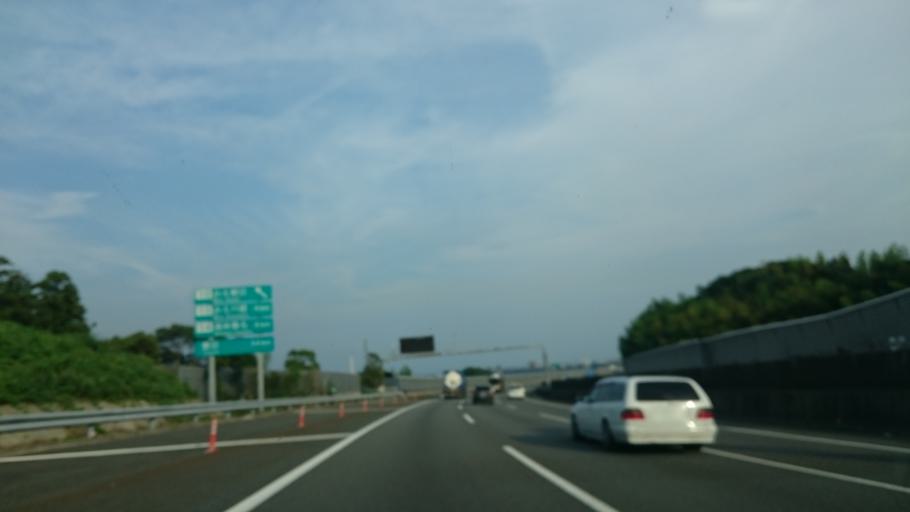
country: JP
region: Mie
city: Yokkaichi
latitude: 35.0347
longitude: 136.6417
